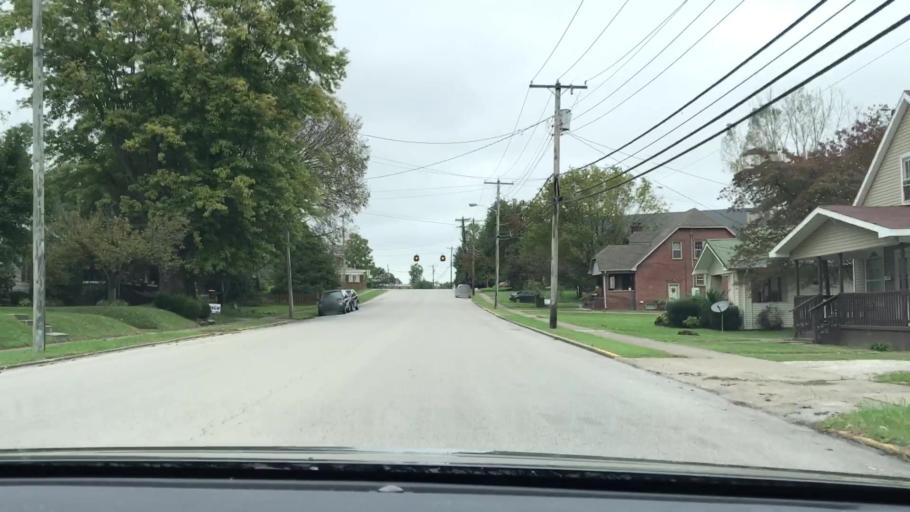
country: US
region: Kentucky
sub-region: Pulaski County
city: Somerset
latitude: 37.0872
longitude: -84.5992
